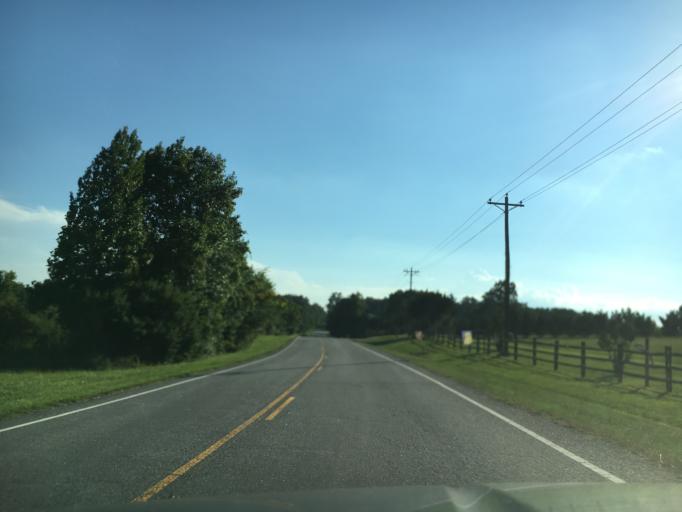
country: US
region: Virginia
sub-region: City of Bedford
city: Bedford
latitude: 37.2241
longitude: -79.5009
